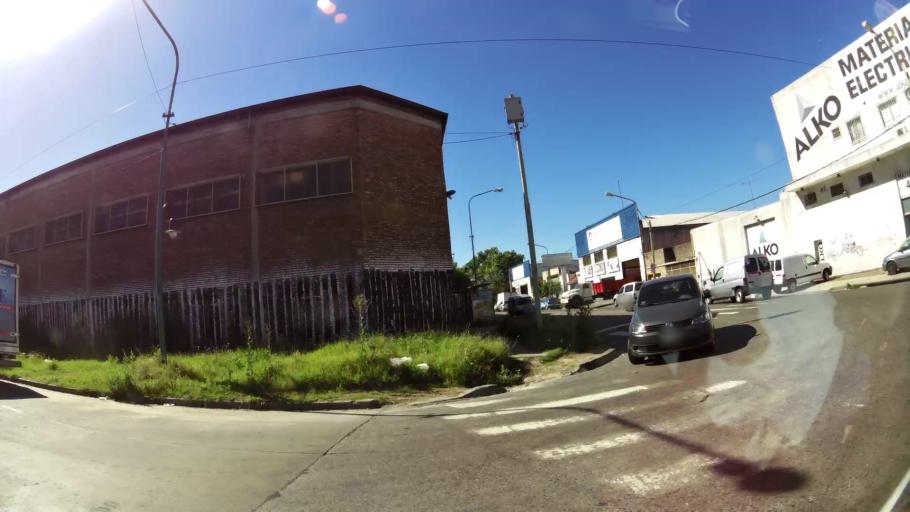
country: AR
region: Buenos Aires
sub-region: Partido de General San Martin
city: General San Martin
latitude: -34.5423
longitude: -58.5289
